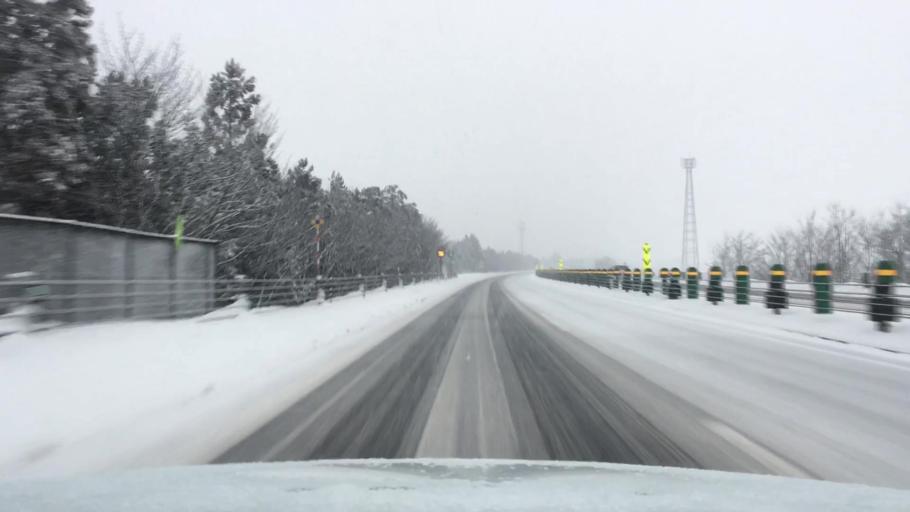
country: JP
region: Akita
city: Hanawa
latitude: 40.2185
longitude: 140.7942
